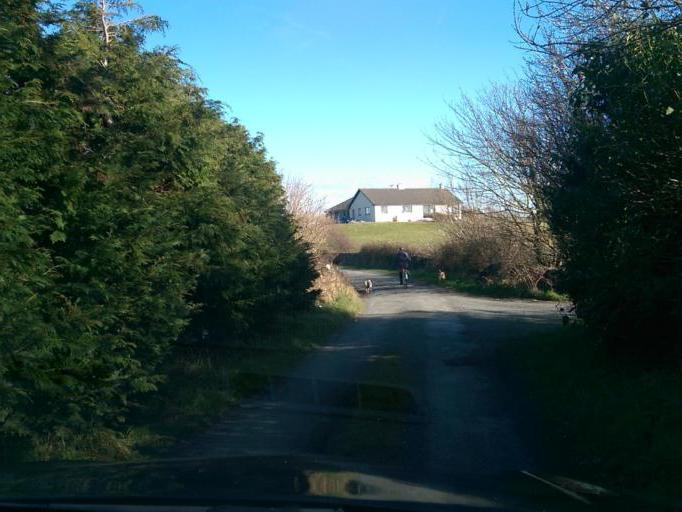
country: IE
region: Connaught
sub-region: County Galway
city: Oranmore
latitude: 53.2371
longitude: -8.9744
